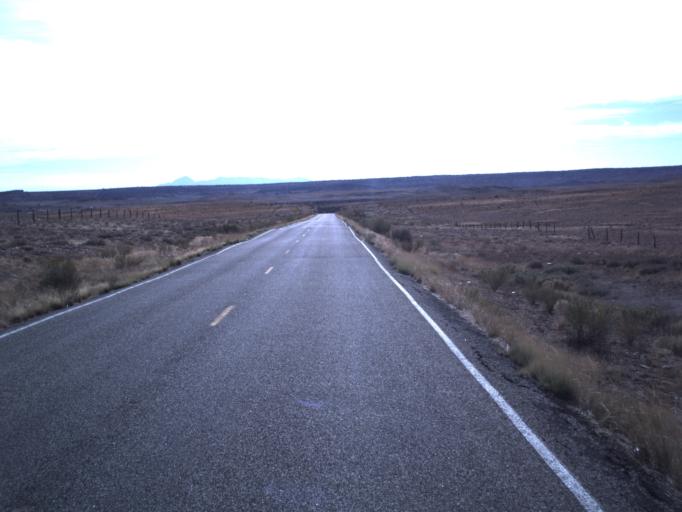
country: US
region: Utah
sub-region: San Juan County
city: Blanding
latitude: 37.4213
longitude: -109.4622
